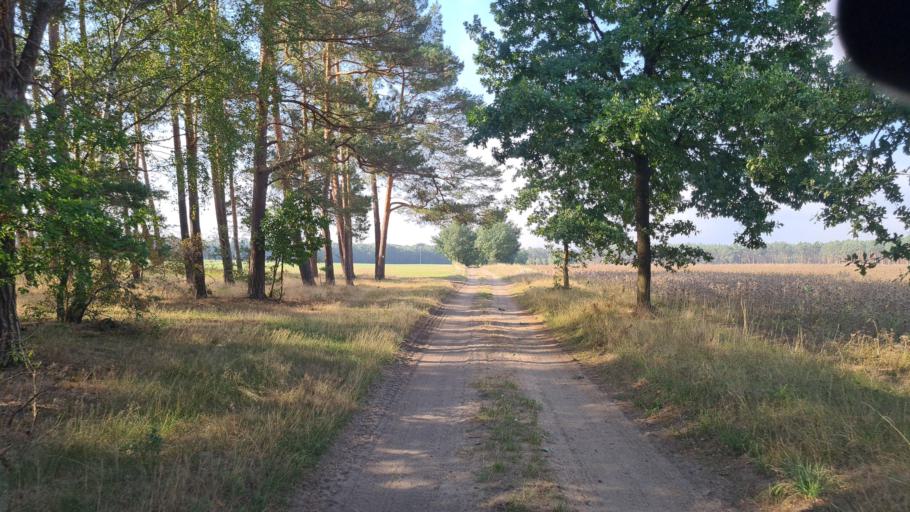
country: DE
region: Brandenburg
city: Belzig
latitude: 52.1669
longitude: 12.6661
